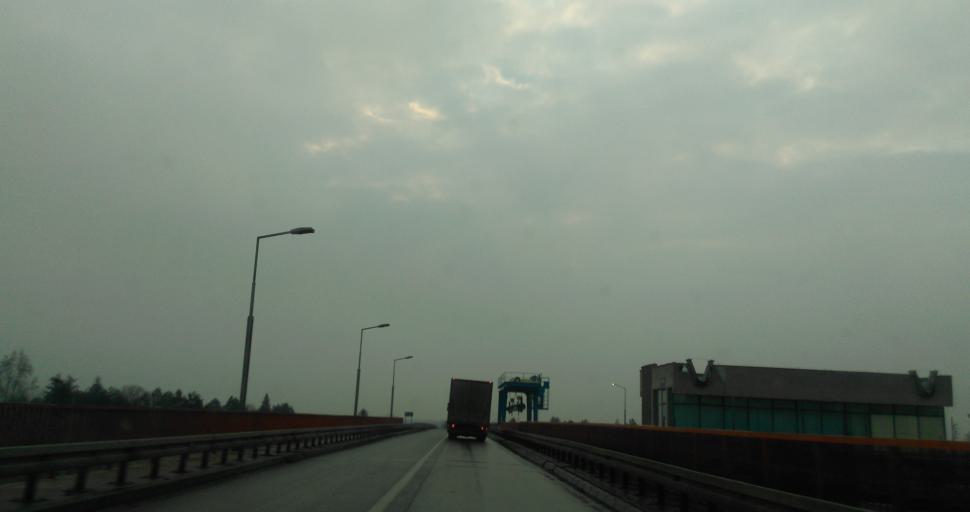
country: RS
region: Autonomna Pokrajina Vojvodina
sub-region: Srednjebanatski Okrug
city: Novi Becej
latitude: 45.5767
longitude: 20.1197
